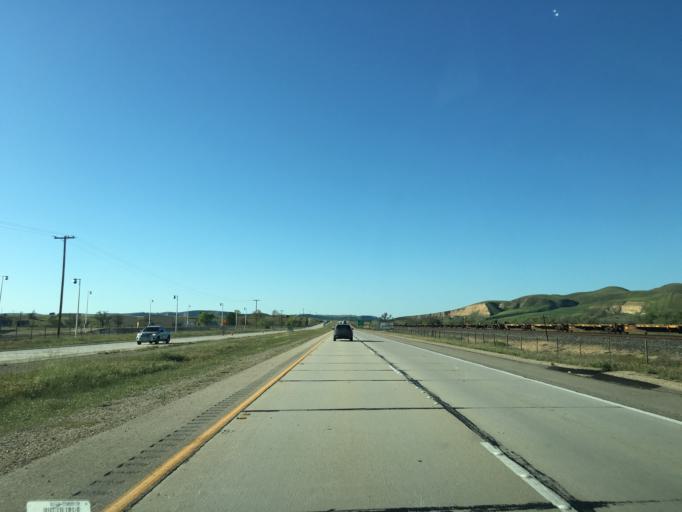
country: US
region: California
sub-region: San Luis Obispo County
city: San Miguel
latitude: 35.7841
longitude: -120.7262
